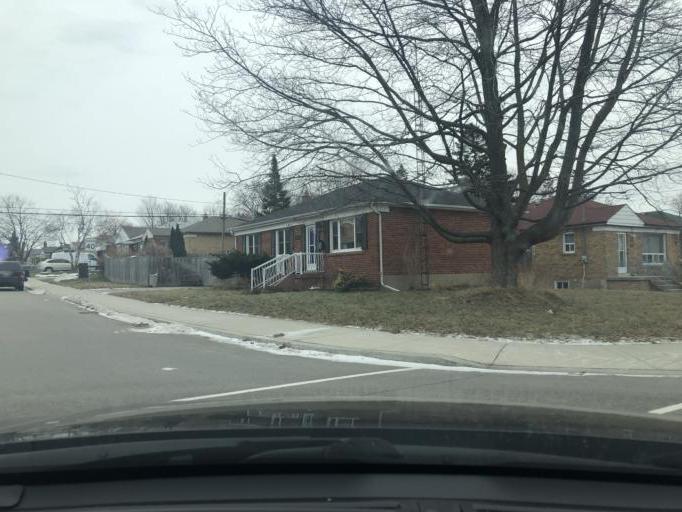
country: CA
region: Ontario
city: Scarborough
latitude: 43.7664
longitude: -79.3072
